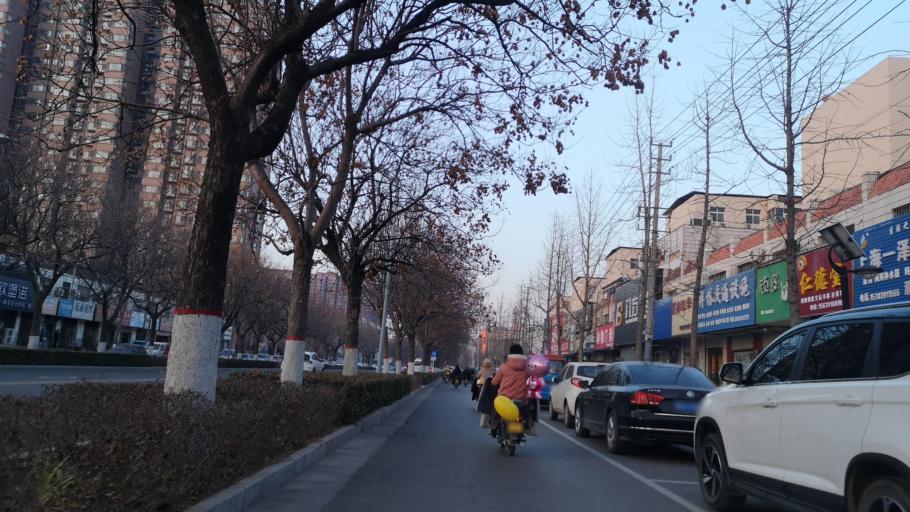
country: CN
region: Henan Sheng
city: Puyang
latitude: 35.7710
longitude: 115.0143
